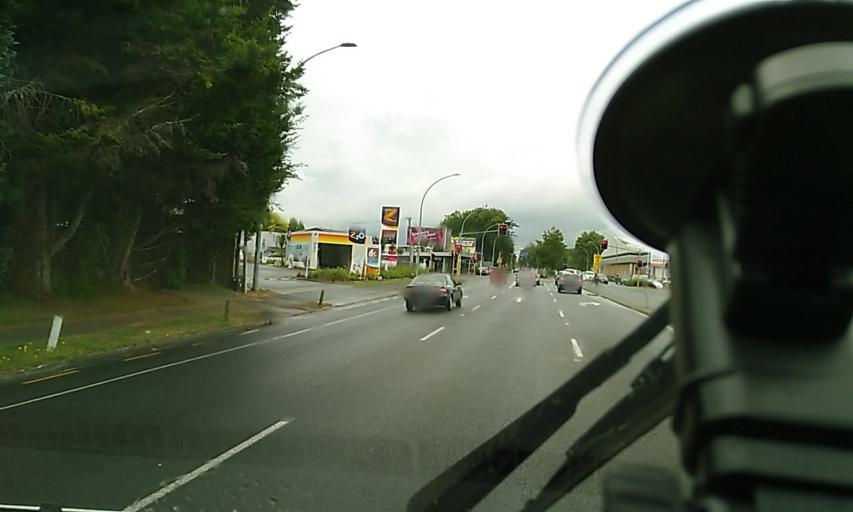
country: NZ
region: Waikato
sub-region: Hamilton City
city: Hamilton
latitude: -37.7811
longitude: 175.2714
